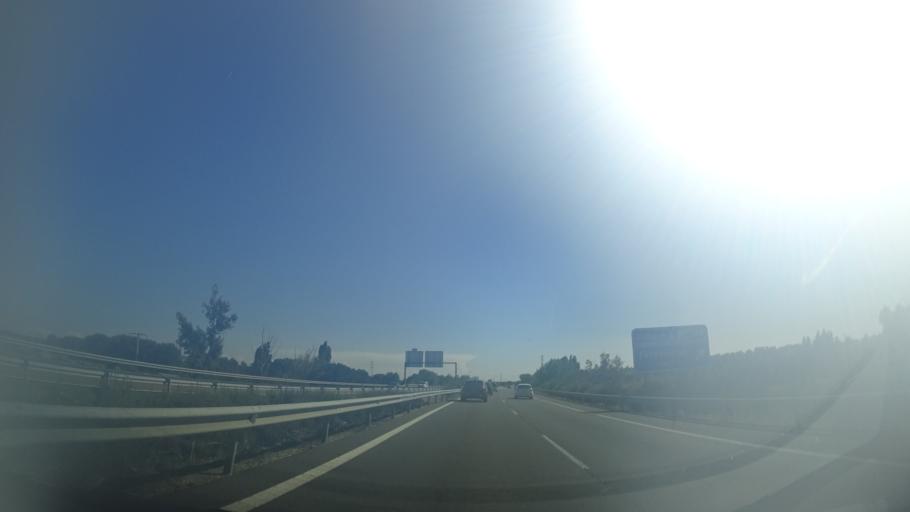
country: ES
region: Castille and Leon
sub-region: Provincia de Valladolid
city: Tordesillas
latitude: 41.4927
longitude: -4.9836
